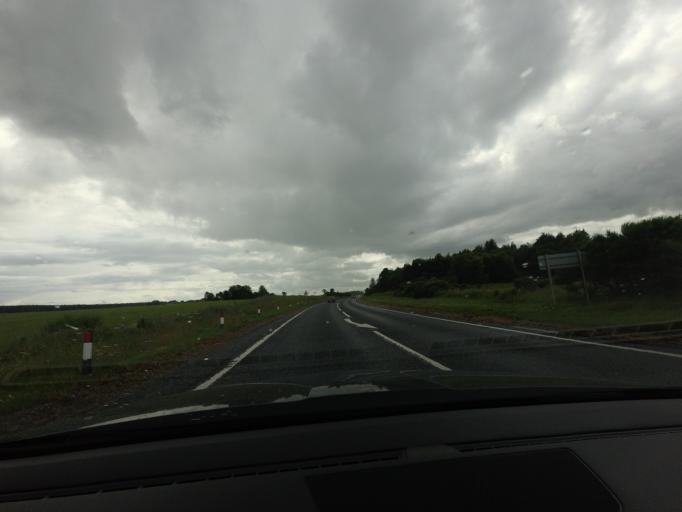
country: GB
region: Scotland
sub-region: Highland
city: Fortrose
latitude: 57.5220
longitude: -4.0646
